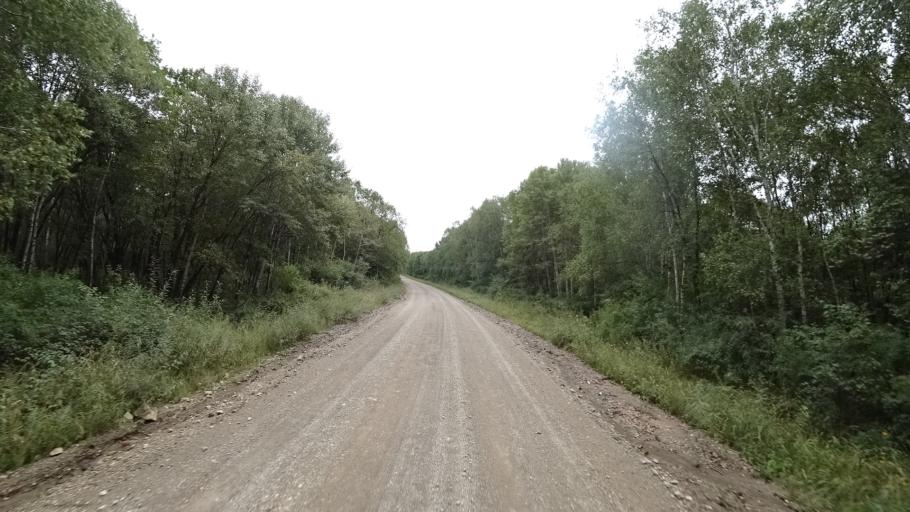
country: RU
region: Primorskiy
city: Ivanovka
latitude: 44.0399
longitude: 132.4961
